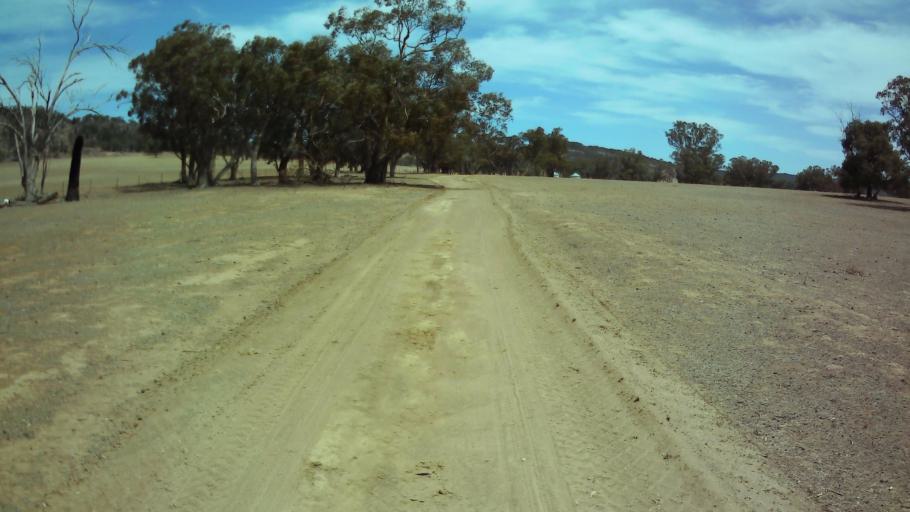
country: AU
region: New South Wales
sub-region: Weddin
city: Grenfell
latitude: -33.7738
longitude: 148.1519
